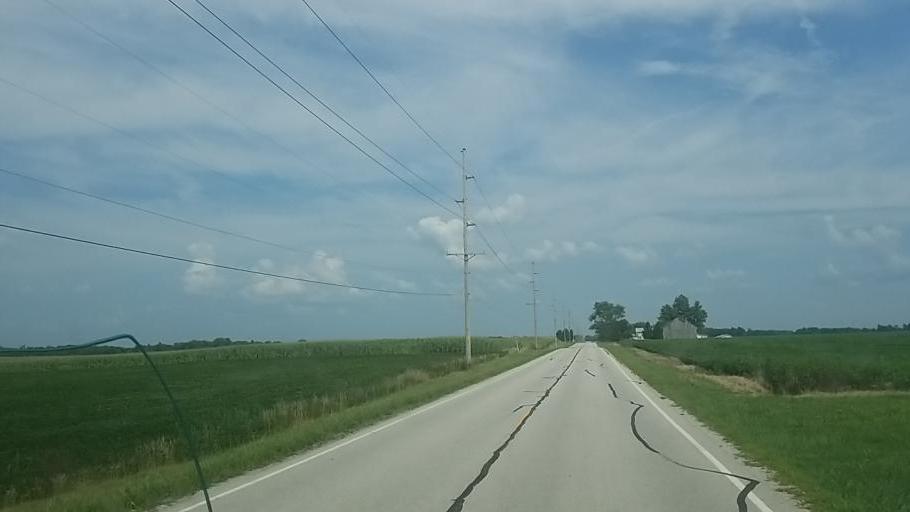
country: US
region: Ohio
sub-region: Hardin County
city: Forest
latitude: 40.7819
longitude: -83.5536
